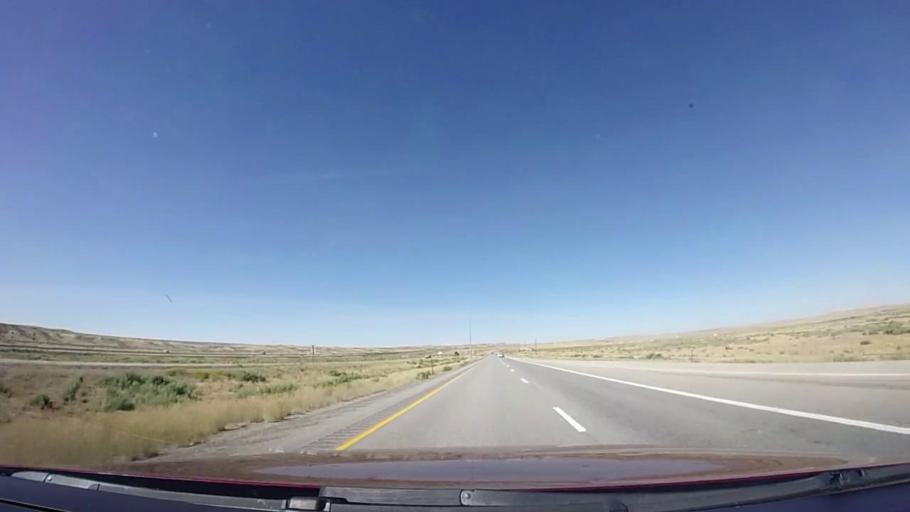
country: US
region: Wyoming
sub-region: Carbon County
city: Rawlins
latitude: 41.6511
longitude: -108.1317
